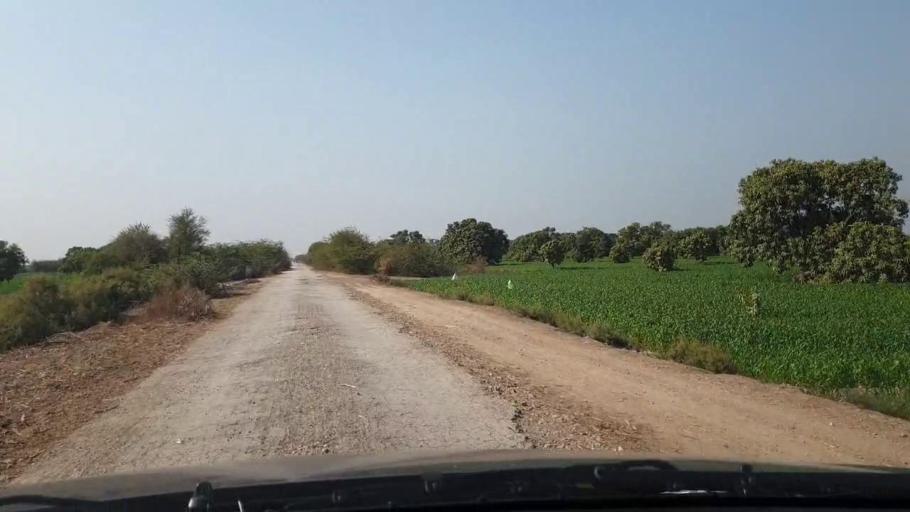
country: PK
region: Sindh
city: Jhol
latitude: 25.8923
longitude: 68.9240
